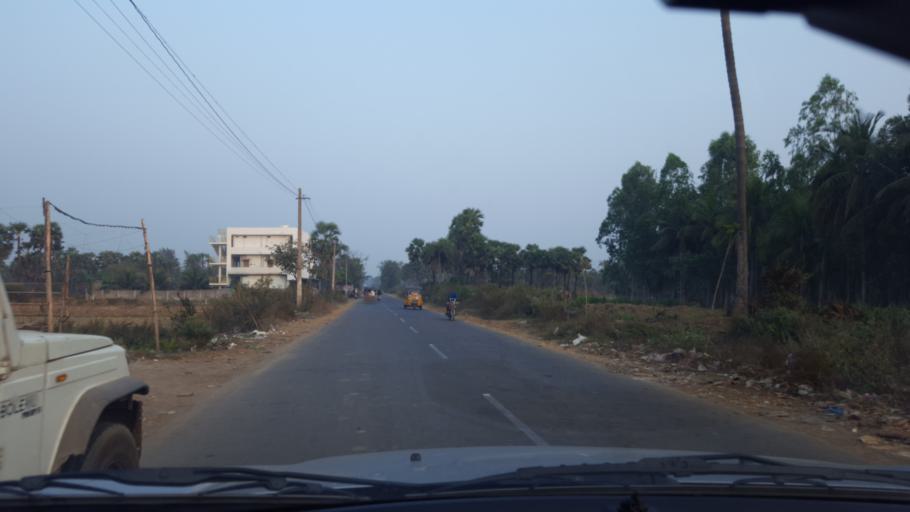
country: IN
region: Andhra Pradesh
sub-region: Srikakulam
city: Amudalavalasa
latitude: 18.3846
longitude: 83.9271
